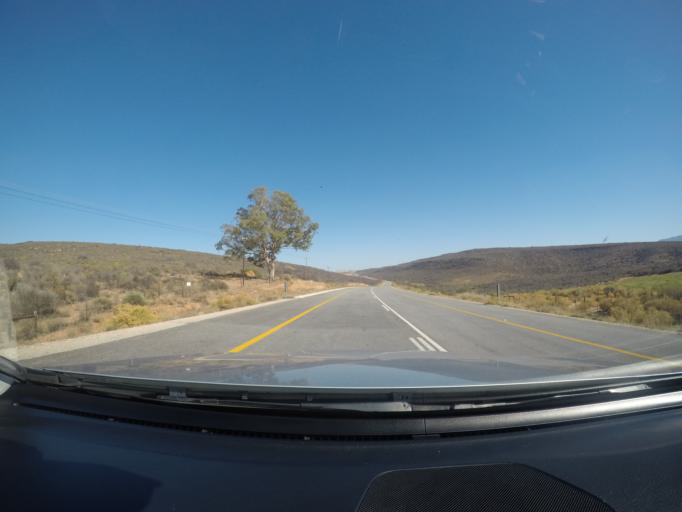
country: ZA
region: Western Cape
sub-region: West Coast District Municipality
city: Clanwilliam
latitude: -32.3180
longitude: 18.9127
